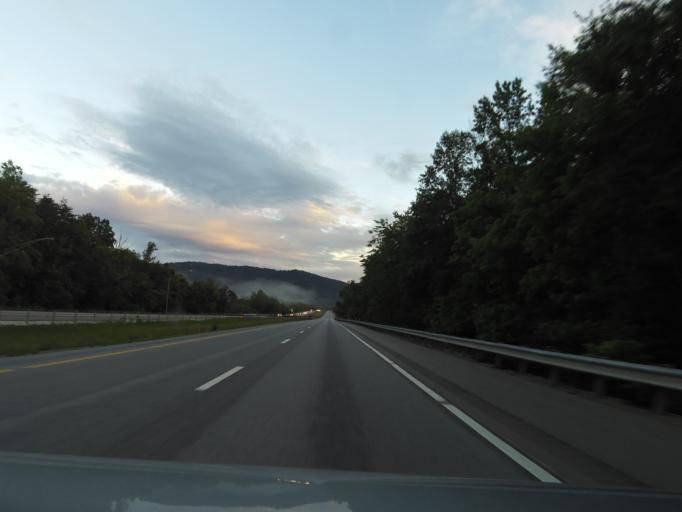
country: US
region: Tennessee
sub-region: Campbell County
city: Jellico
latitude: 36.6128
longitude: -84.1065
